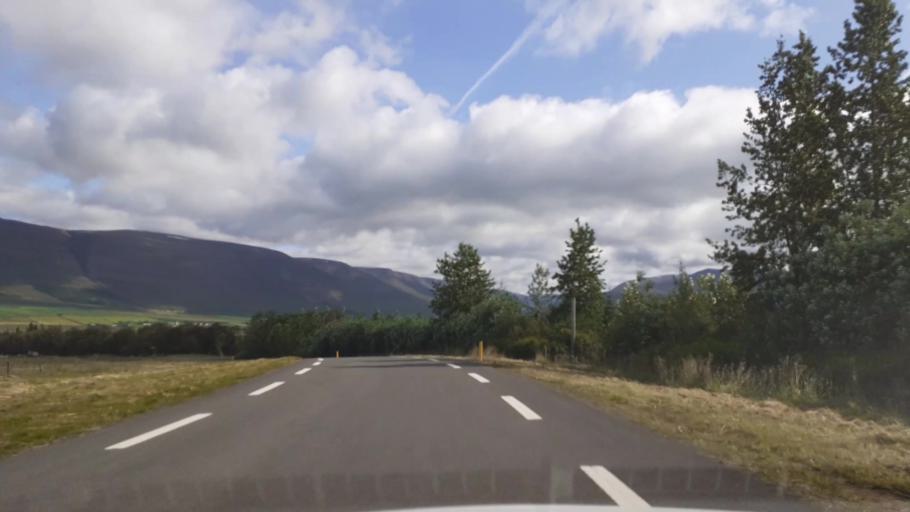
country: IS
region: Northeast
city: Akureyri
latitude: 65.6494
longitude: -18.0907
